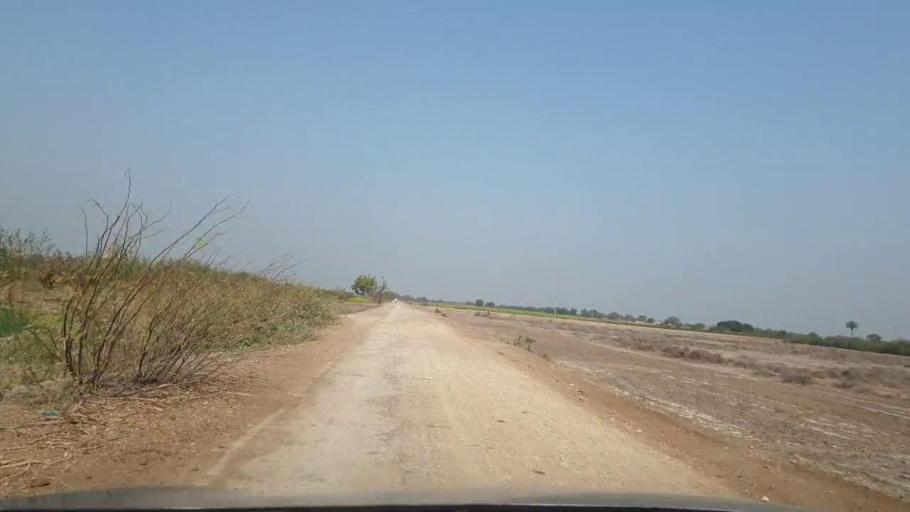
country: PK
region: Sindh
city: Tando Allahyar
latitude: 25.5422
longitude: 68.8141
